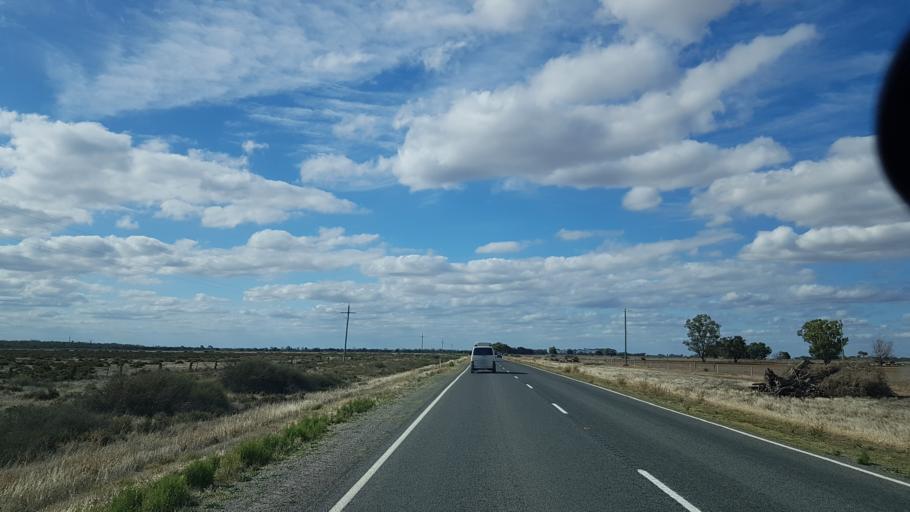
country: AU
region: Victoria
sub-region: Swan Hill
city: Swan Hill
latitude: -35.8361
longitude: 143.9418
